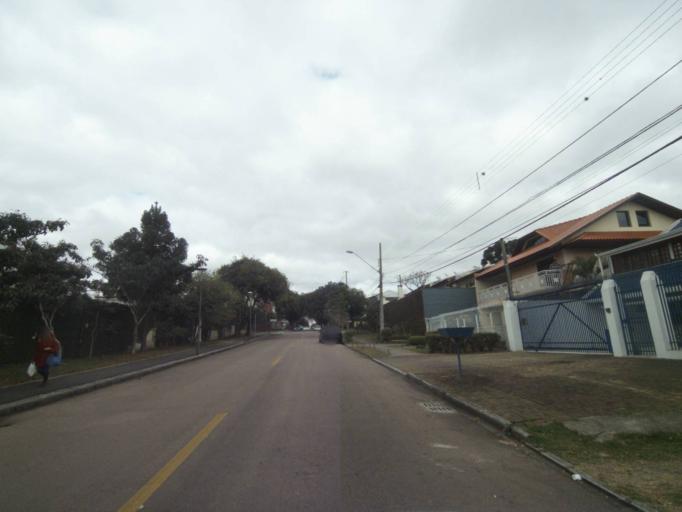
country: BR
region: Parana
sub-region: Curitiba
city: Curitiba
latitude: -25.4569
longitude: -49.2836
